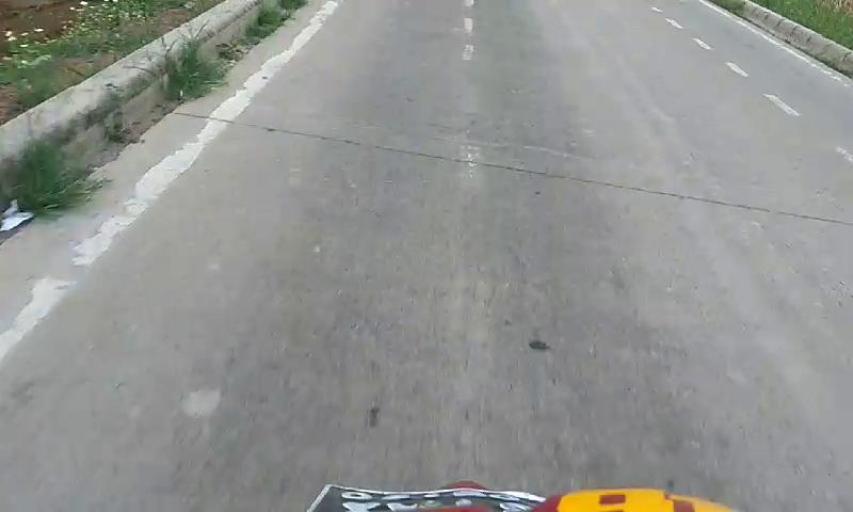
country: ID
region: West Java
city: Bekasi
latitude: -6.1462
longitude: 106.9702
